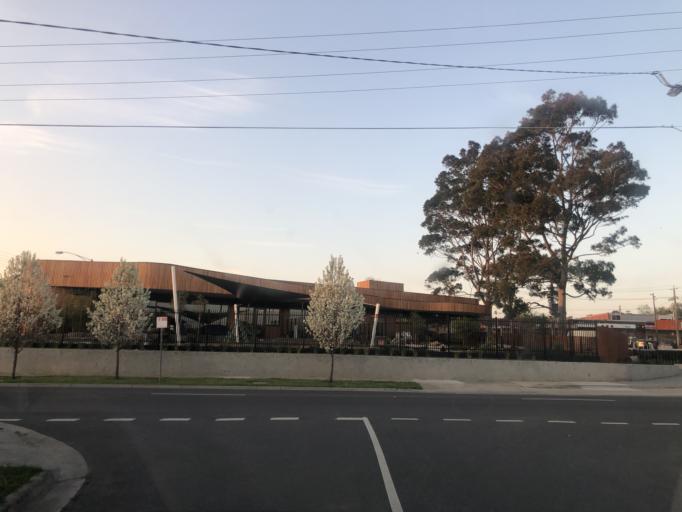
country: AU
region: Victoria
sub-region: Casey
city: Doveton
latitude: -37.9954
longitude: 145.2390
